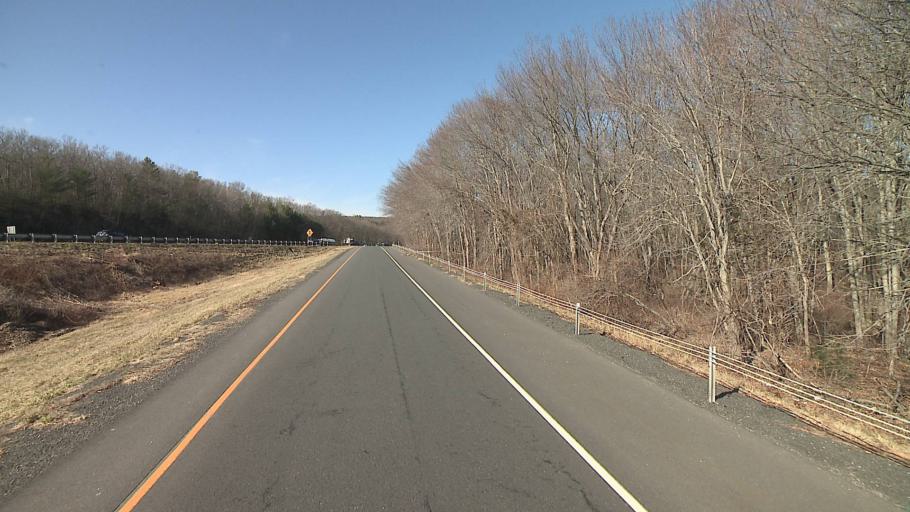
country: US
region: Connecticut
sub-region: Hartford County
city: Terramuggus
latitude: 41.6505
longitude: -72.4866
